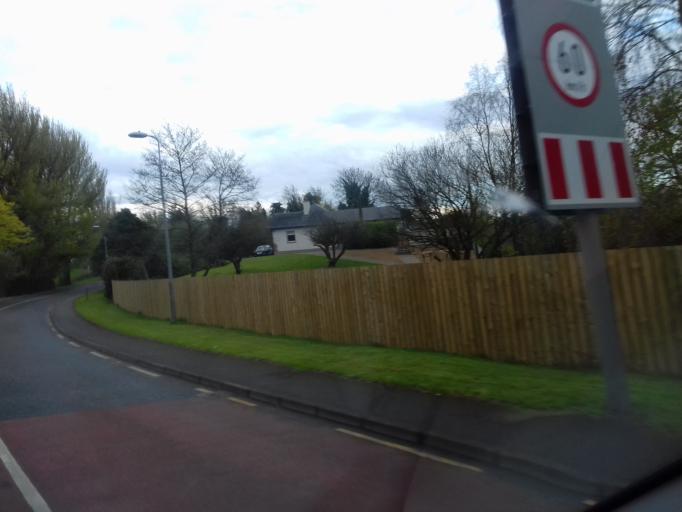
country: IE
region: Ulster
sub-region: An Cabhan
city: Ballyconnell
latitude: 54.1190
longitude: -7.5918
